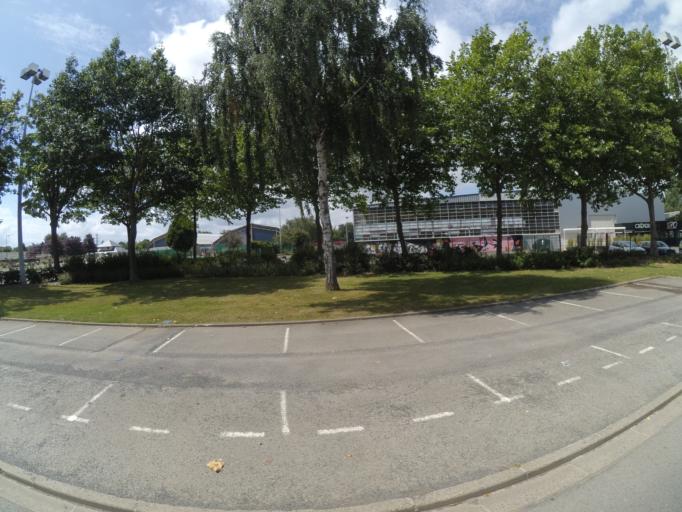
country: FR
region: Brittany
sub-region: Departement des Cotes-d'Armor
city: Saint-Brieuc
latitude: 48.4979
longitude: -2.7652
